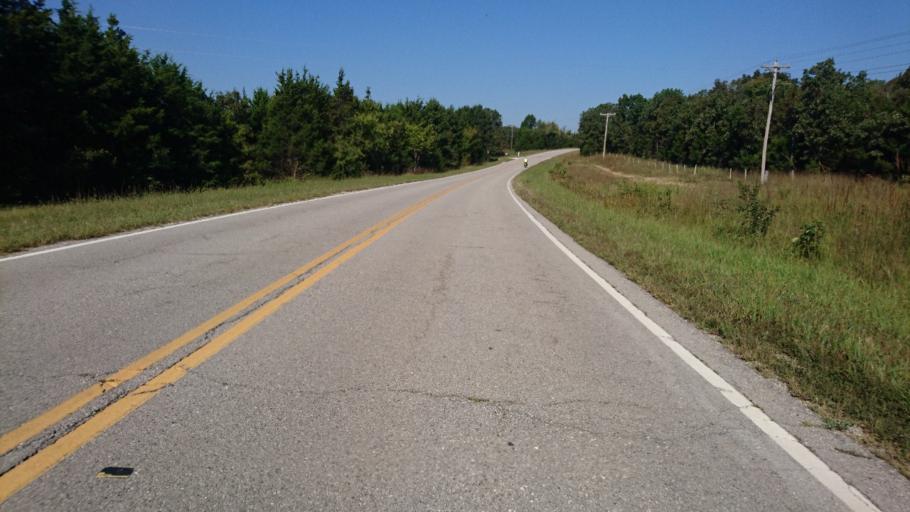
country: US
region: Missouri
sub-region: Pulaski County
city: Richland
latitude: 37.7525
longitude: -92.3708
